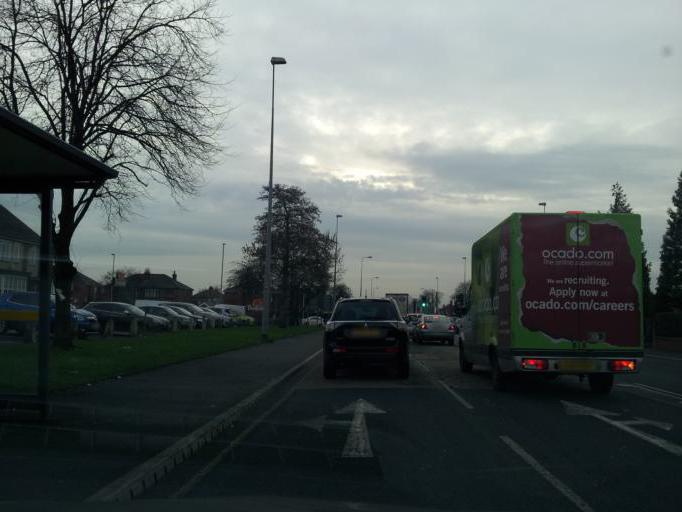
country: GB
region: England
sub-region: Manchester
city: Failsworth
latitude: 53.5230
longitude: -2.1647
